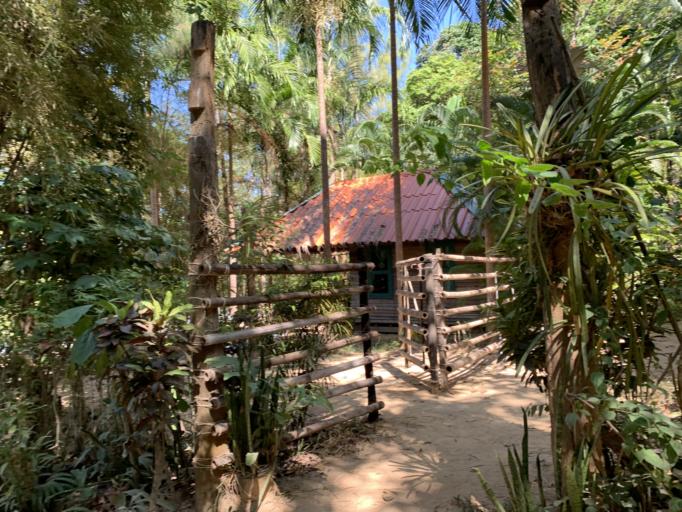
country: TH
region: Ranong
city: Kapoe
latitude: 9.7701
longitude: 98.4114
